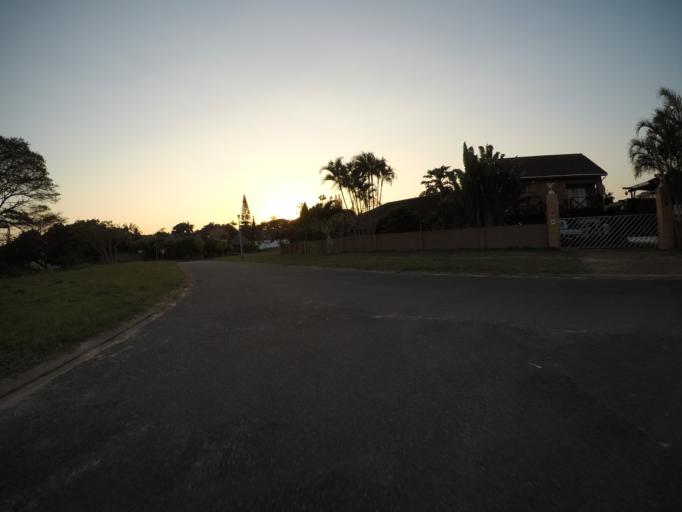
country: ZA
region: KwaZulu-Natal
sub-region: uThungulu District Municipality
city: Richards Bay
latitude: -28.7686
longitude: 32.1239
